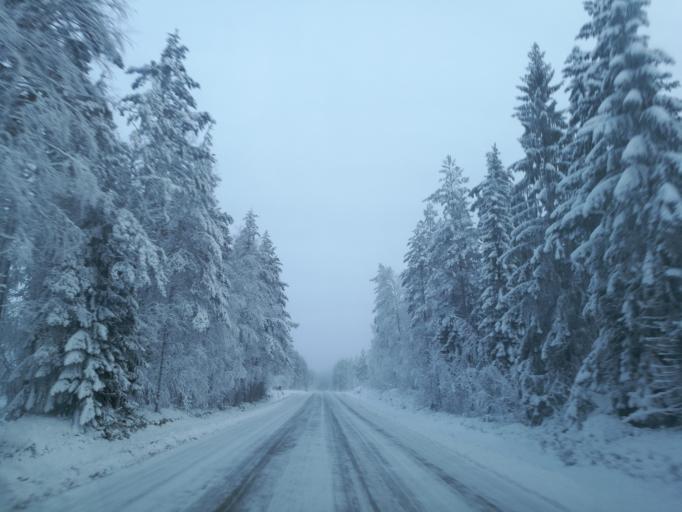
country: NO
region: Hedmark
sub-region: Grue
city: Kirkenaer
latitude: 60.4625
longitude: 12.5361
